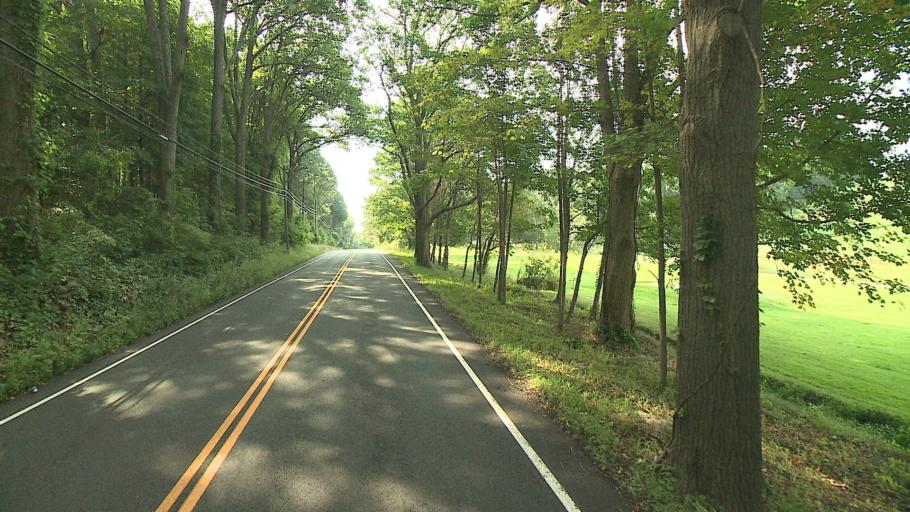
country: US
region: Connecticut
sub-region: Fairfield County
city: Bethel
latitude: 41.3195
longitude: -73.3859
